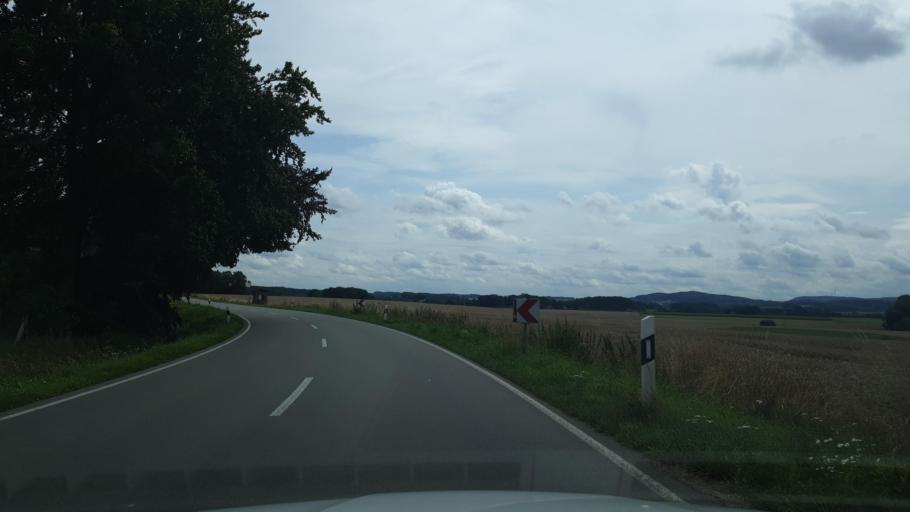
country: DE
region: Lower Saxony
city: Dissen
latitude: 52.1831
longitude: 8.2155
